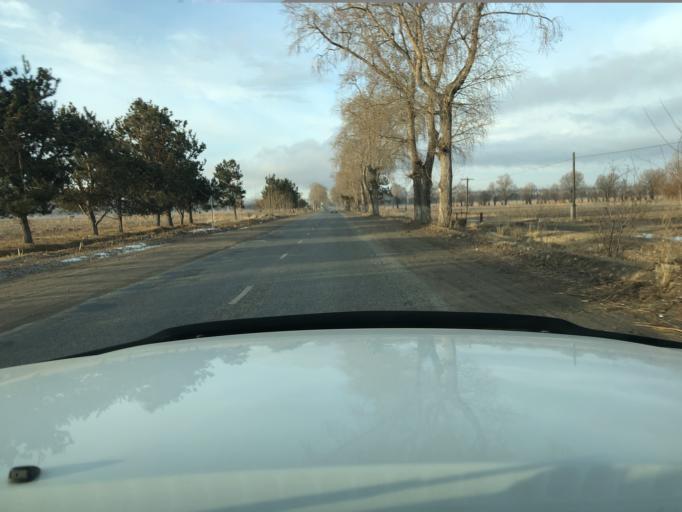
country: KG
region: Ysyk-Koel
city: Karakol
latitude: 42.4810
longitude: 78.3484
